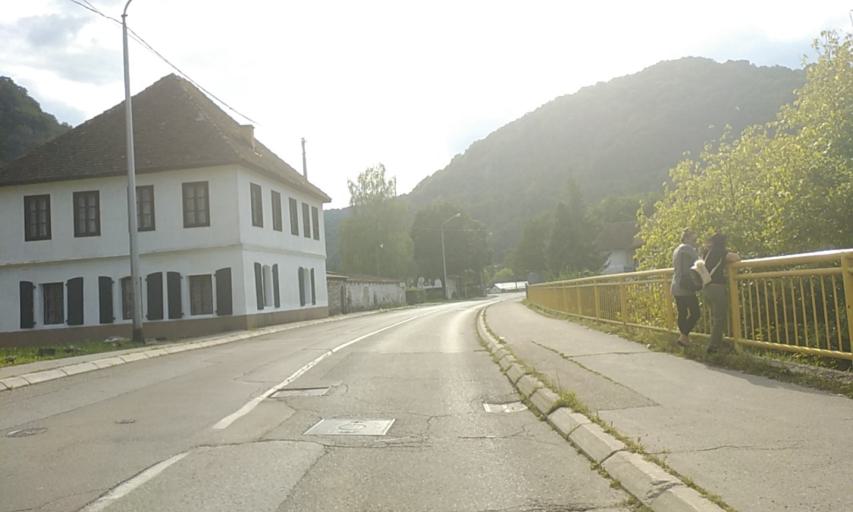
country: BA
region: Republika Srpska
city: Hiseti
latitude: 44.7488
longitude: 17.1589
